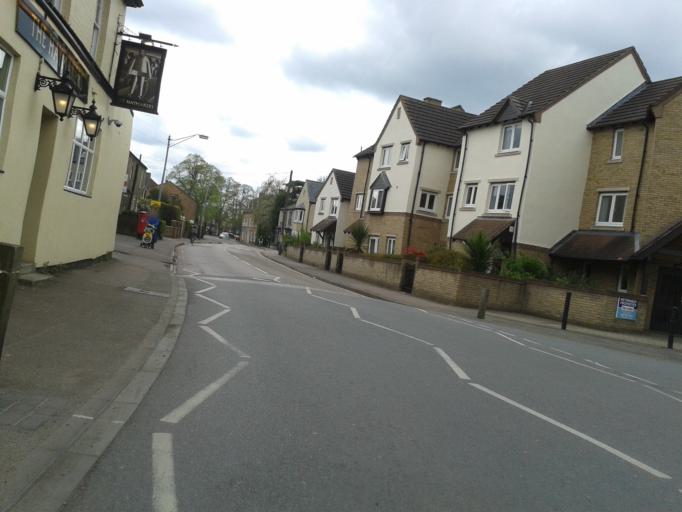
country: GB
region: England
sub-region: Cambridgeshire
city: Cambridge
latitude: 52.2176
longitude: 0.1395
